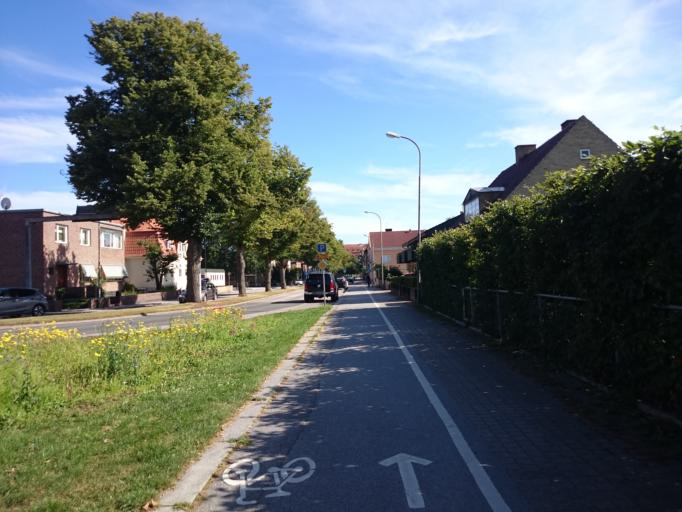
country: SE
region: Blekinge
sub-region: Karlshamns Kommun
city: Karlshamn
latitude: 56.1691
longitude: 14.8696
